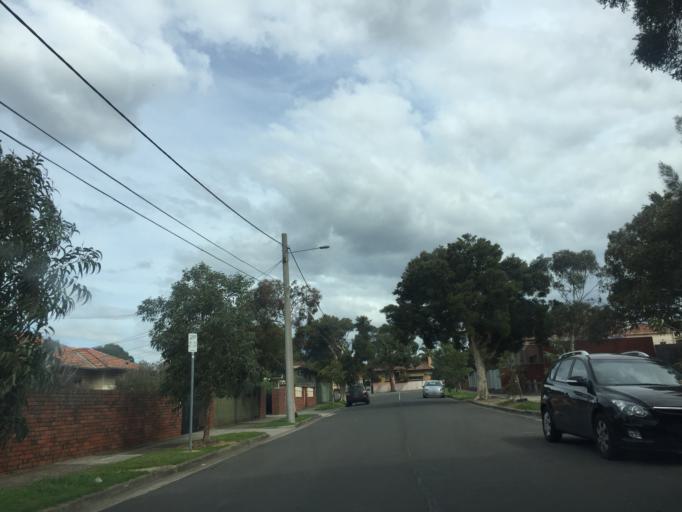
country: AU
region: Victoria
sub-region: Darebin
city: Preston
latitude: -37.7489
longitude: 145.0094
